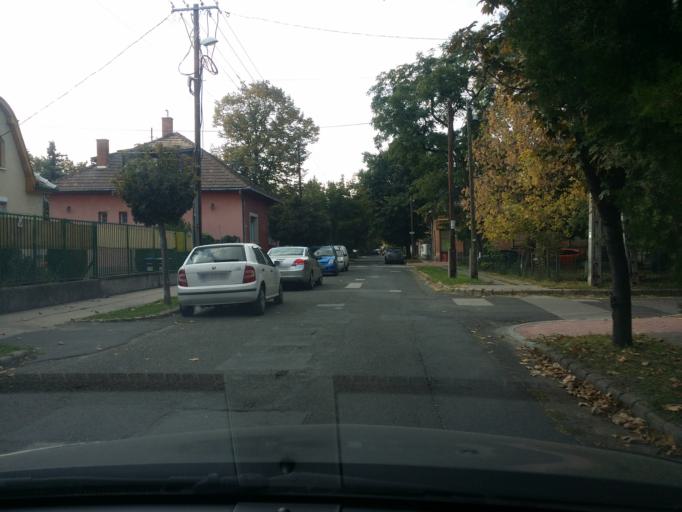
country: HU
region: Budapest
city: Budapest IV. keruelet
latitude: 47.5718
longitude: 19.0988
